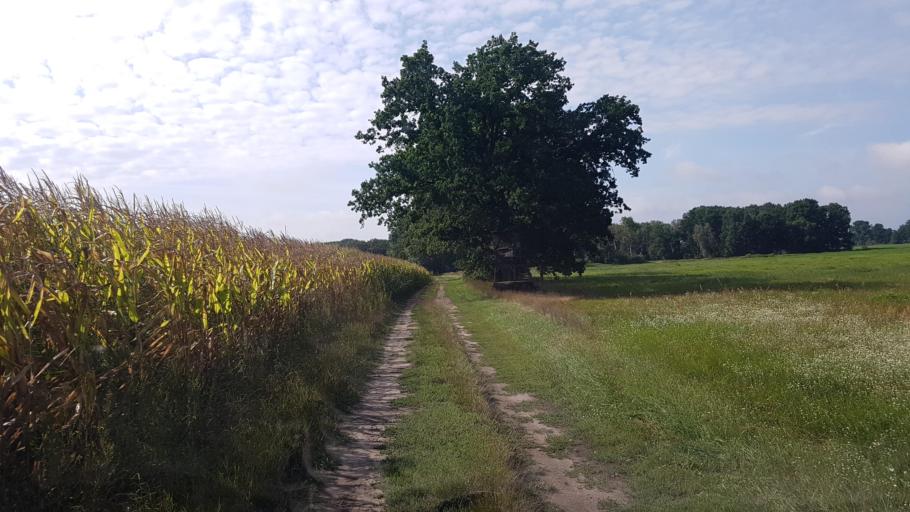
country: DE
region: Brandenburg
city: Hohenbucko
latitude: 51.7212
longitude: 13.4836
